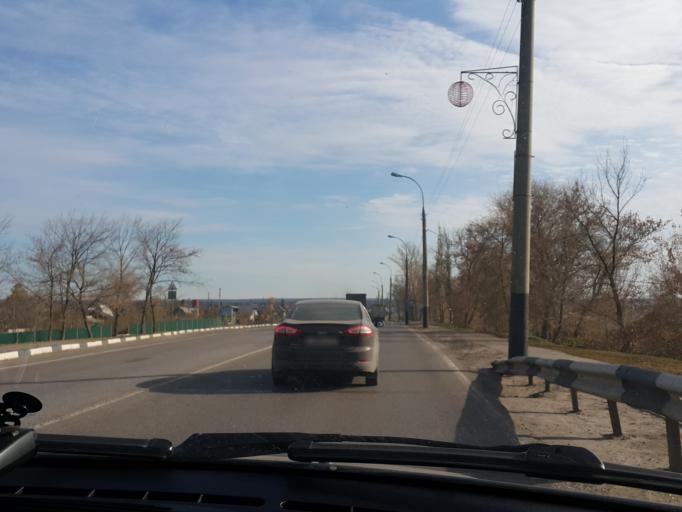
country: RU
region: Tambov
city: Tambov
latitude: 52.7223
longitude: 41.4822
